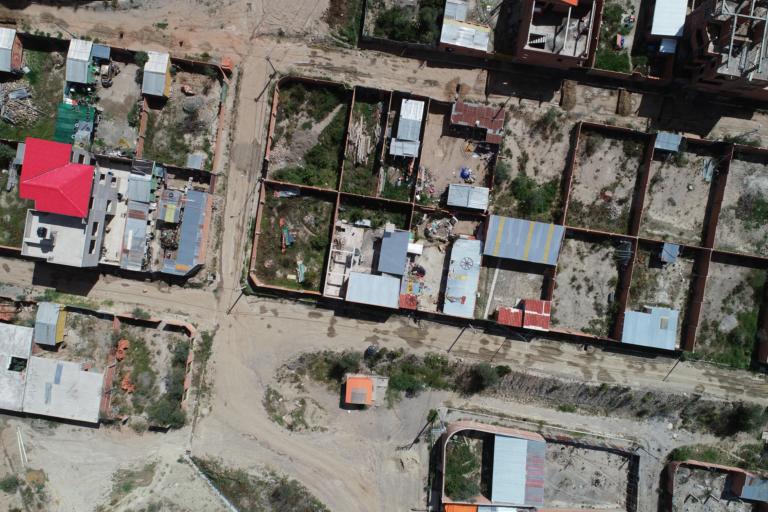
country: BO
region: La Paz
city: La Paz
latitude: -16.5159
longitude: -68.1044
